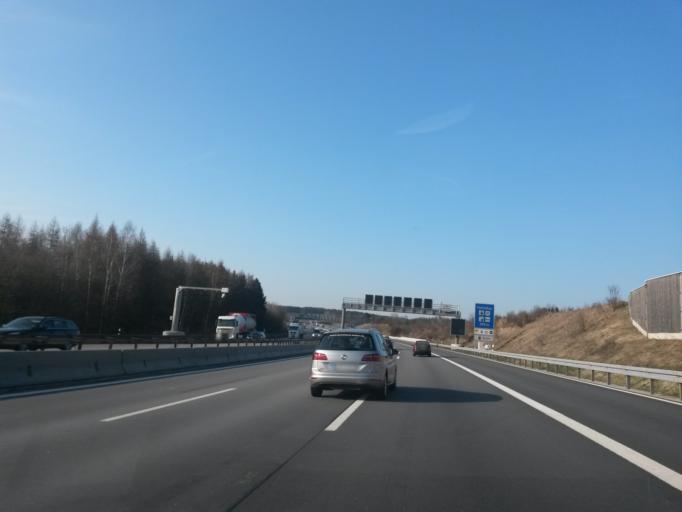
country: DE
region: Bavaria
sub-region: Upper Bavaria
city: Schweitenkirchen
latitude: 48.5467
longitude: 11.5940
